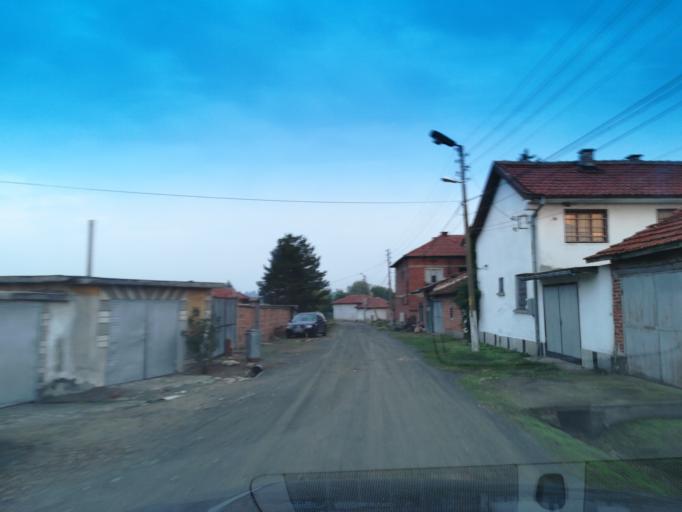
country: BG
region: Stara Zagora
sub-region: Obshtina Chirpan
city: Chirpan
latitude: 42.1718
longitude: 25.2070
